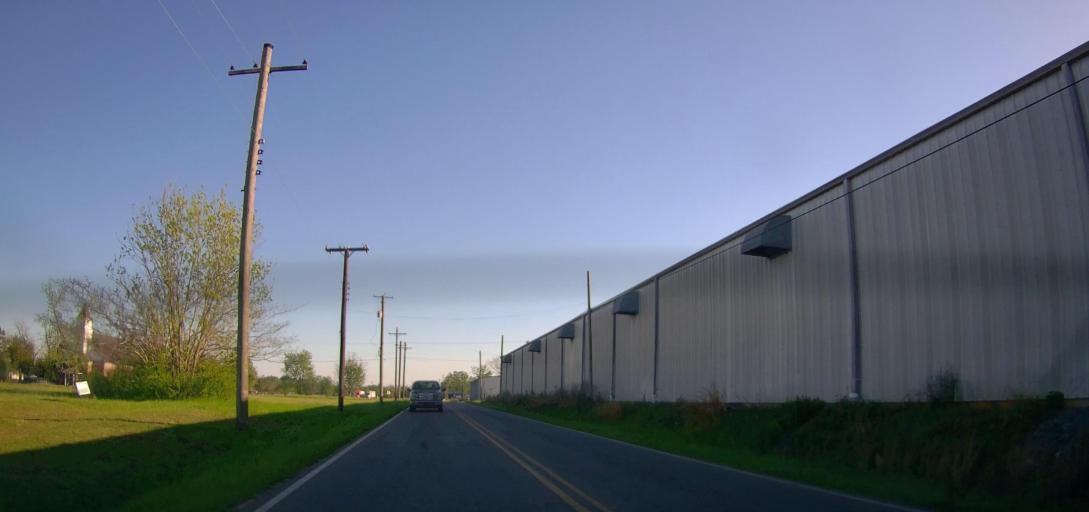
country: US
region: Georgia
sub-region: Ben Hill County
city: Fitzgerald
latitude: 31.7184
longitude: -83.2440
